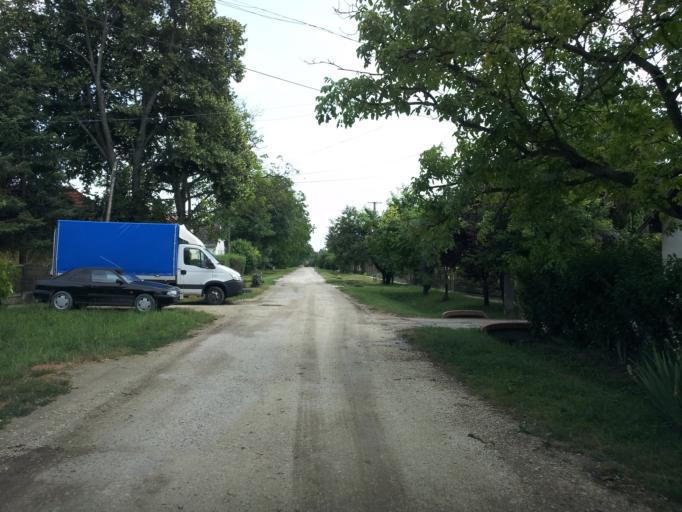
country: HU
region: Fejer
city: Enying
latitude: 46.9407
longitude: 18.2390
